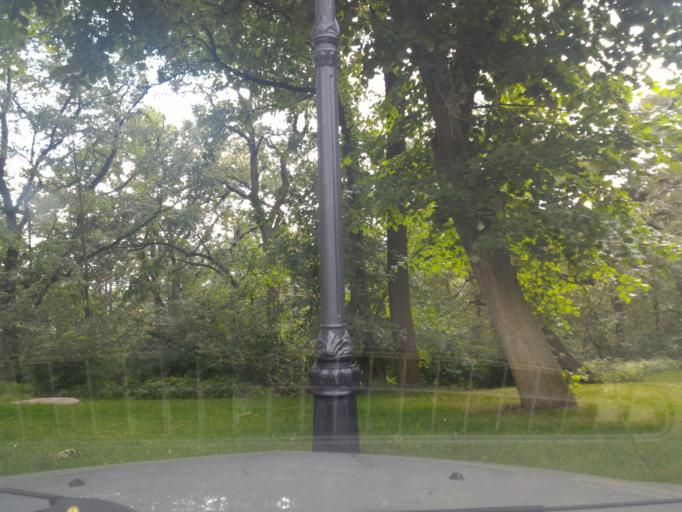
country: CZ
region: Central Bohemia
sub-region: Okres Kutna Hora
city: Kutna Hora
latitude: 49.9708
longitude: 15.2849
